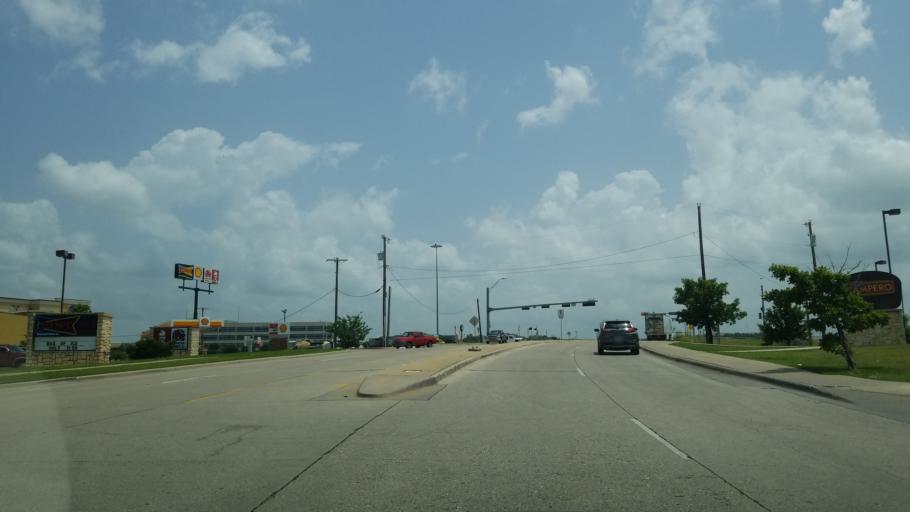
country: US
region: Texas
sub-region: Dallas County
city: Cockrell Hill
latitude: 32.7686
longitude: -96.8961
